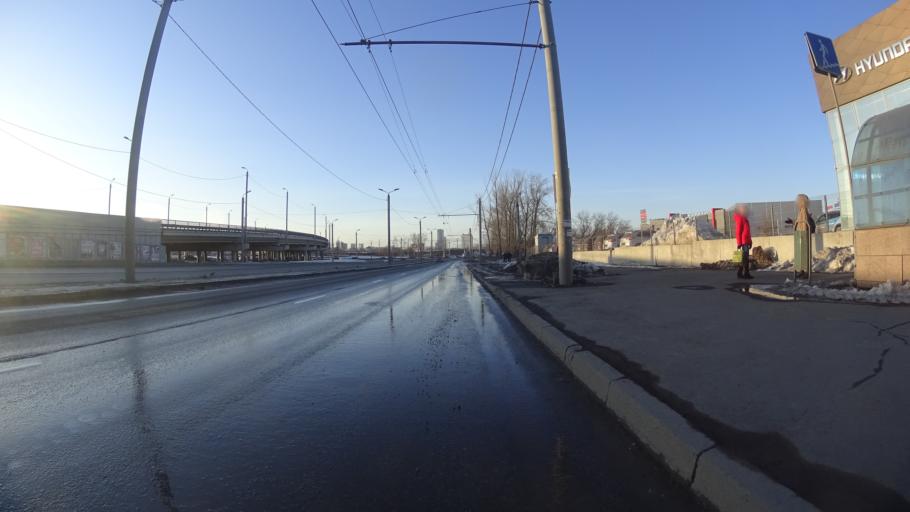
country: RU
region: Chelyabinsk
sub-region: Gorod Chelyabinsk
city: Chelyabinsk
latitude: 55.1495
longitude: 61.4446
